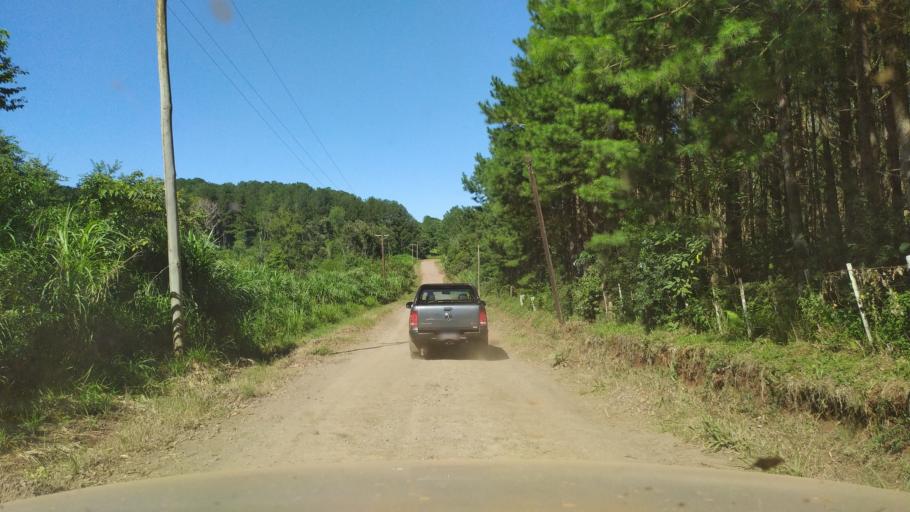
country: AR
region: Misiones
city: Caraguatay
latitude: -26.6831
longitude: -54.7104
